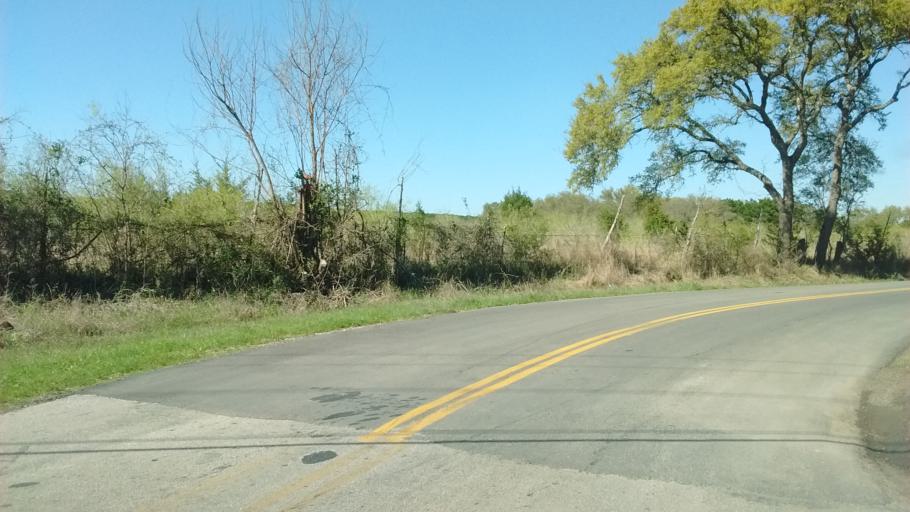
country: US
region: Texas
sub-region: Comal County
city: New Braunfels
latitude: 29.7150
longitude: -98.2118
